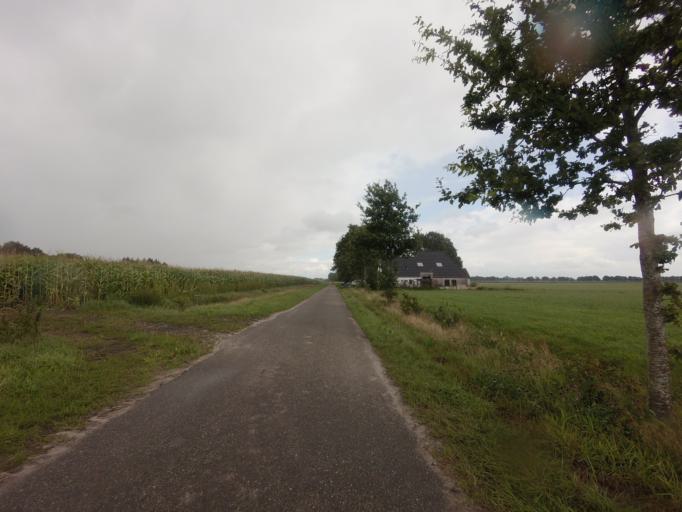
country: NL
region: Drenthe
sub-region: Gemeente Westerveld
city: Dwingeloo
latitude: 52.9750
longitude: 6.3475
